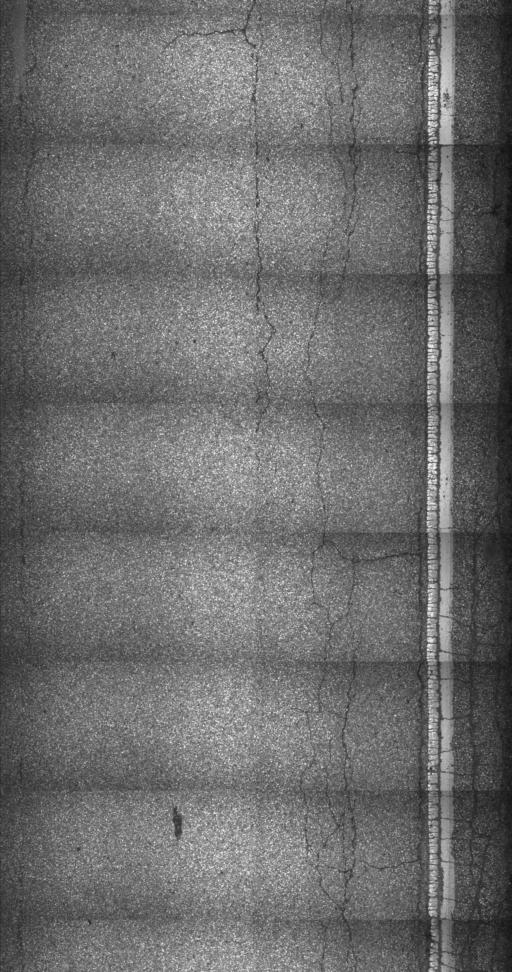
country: US
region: Vermont
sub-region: Orange County
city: Randolph
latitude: 43.8480
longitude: -72.7999
